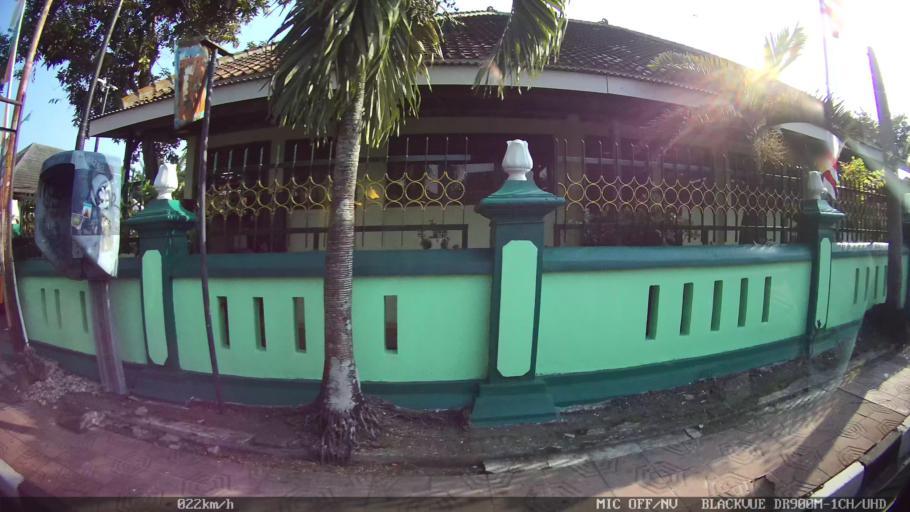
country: ID
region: Daerah Istimewa Yogyakarta
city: Yogyakarta
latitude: -7.8091
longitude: 110.3679
